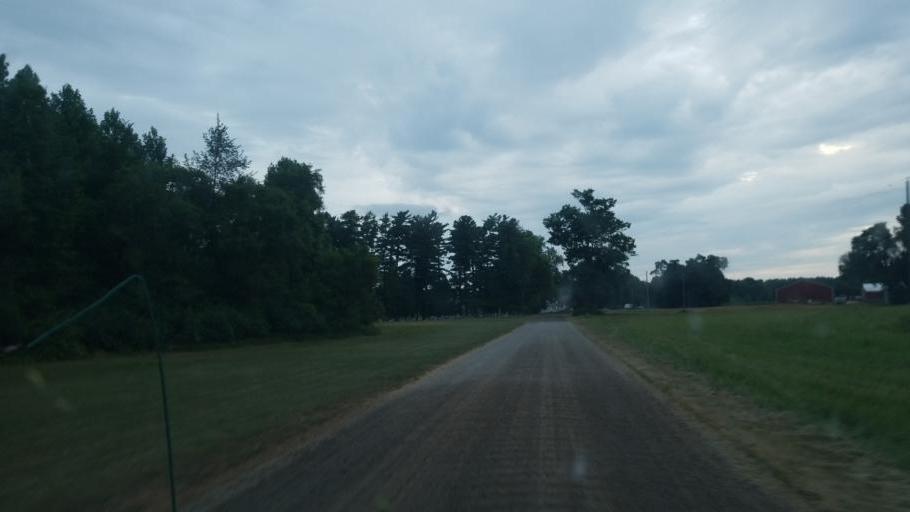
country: US
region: Ohio
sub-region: Defiance County
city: Hicksville
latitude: 41.3417
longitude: -84.8396
